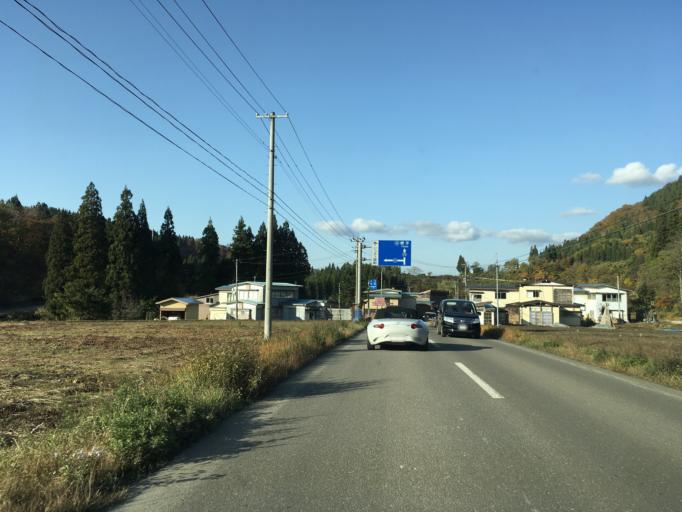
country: JP
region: Akita
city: Yuzawa
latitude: 39.0842
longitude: 140.7182
